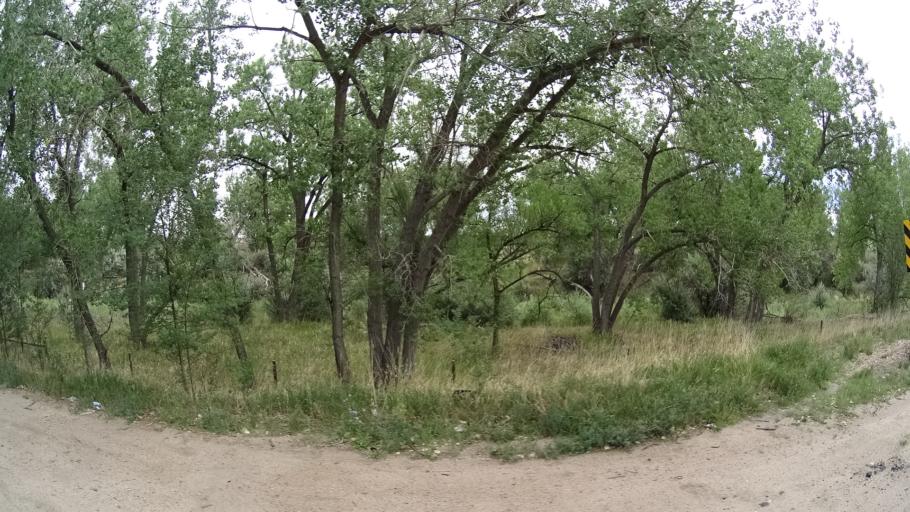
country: US
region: Colorado
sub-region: El Paso County
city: Fountain
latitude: 38.6739
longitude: -104.6968
